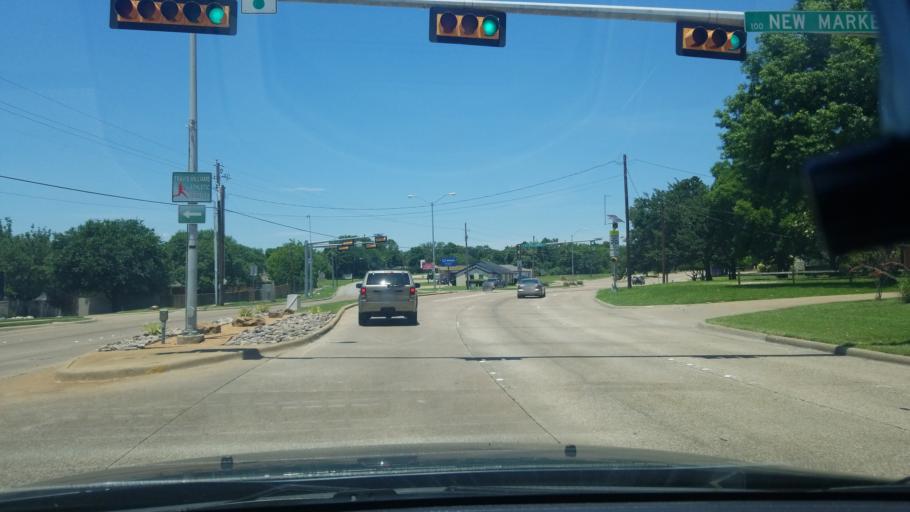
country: US
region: Texas
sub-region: Dallas County
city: Mesquite
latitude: 32.7559
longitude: -96.5970
